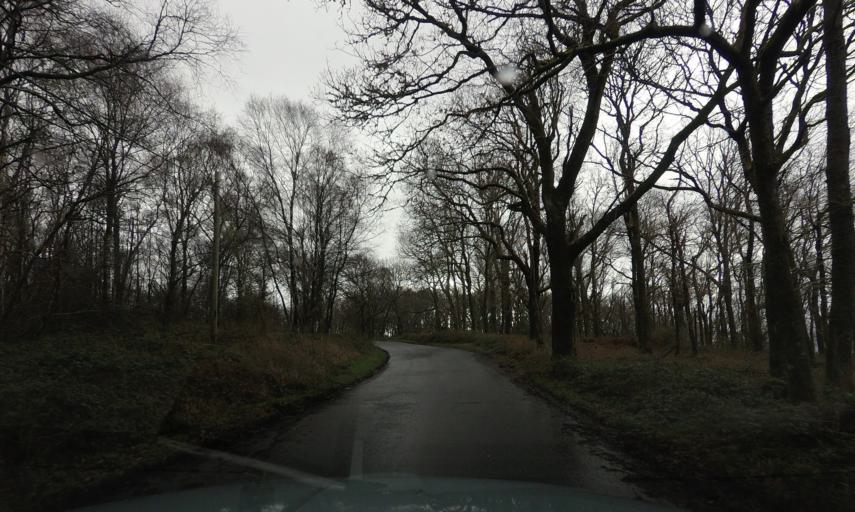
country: GB
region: Scotland
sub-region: West Dunbartonshire
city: Balloch
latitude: 56.1233
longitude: -4.5987
